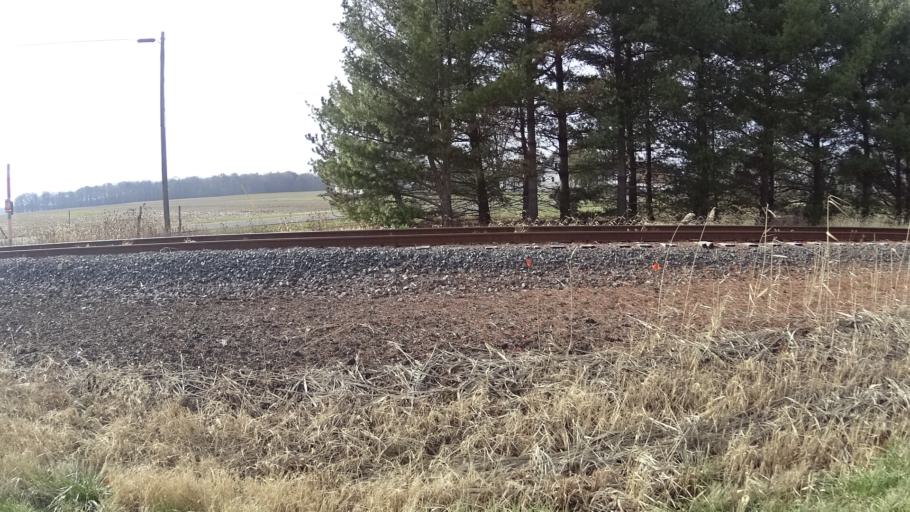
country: US
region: Ohio
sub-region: Lorain County
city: Grafton
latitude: 41.2076
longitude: -81.9841
